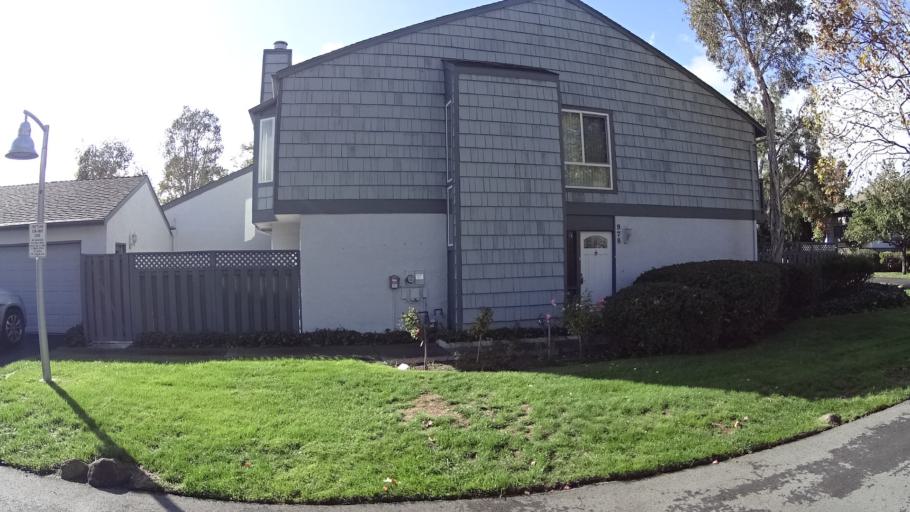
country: US
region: California
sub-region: San Mateo County
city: Foster City
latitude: 37.5506
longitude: -122.2658
